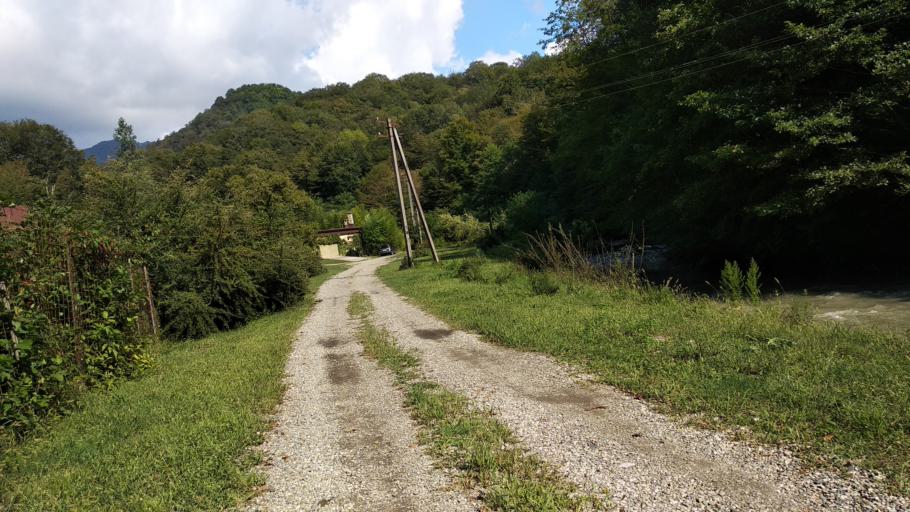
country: RU
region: Krasnodarskiy
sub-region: Sochi City
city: Sochi
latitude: 43.6351
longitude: 39.8220
